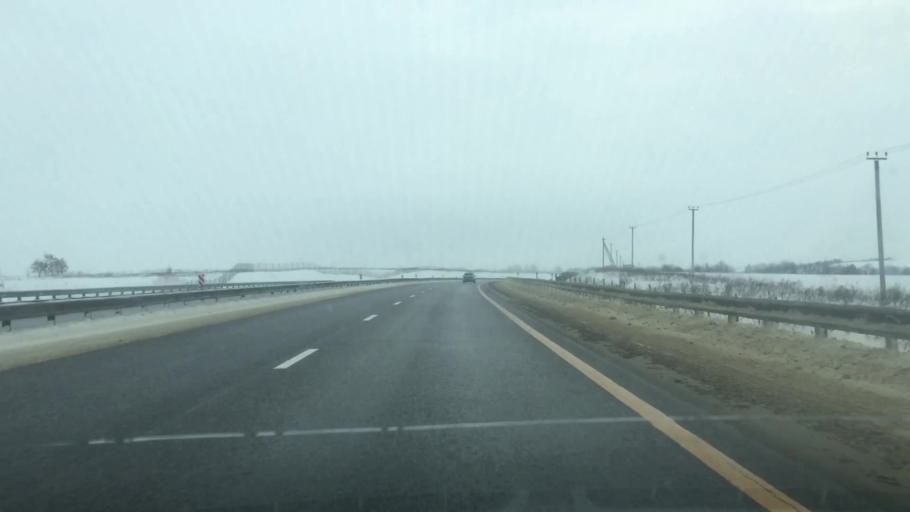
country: RU
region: Tula
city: Yefremov
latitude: 53.1413
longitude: 38.2468
